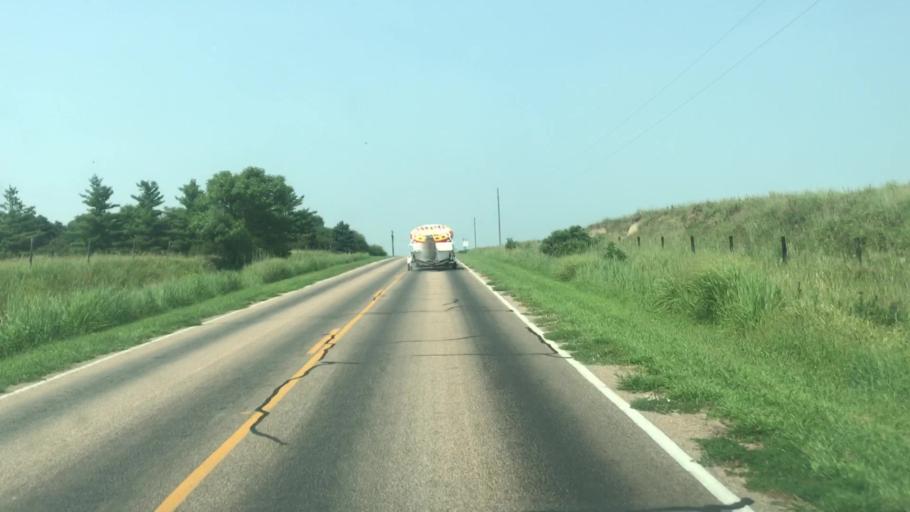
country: US
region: Nebraska
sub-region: Sherman County
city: Loup City
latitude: 41.2836
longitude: -98.8998
